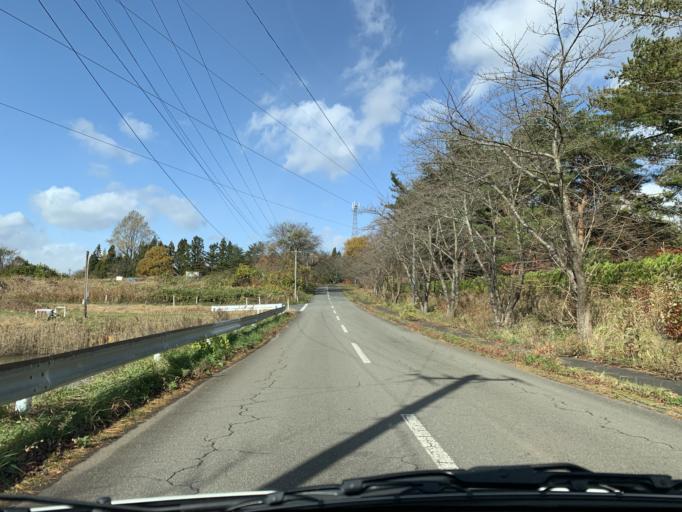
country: JP
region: Iwate
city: Mizusawa
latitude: 39.0366
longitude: 141.0840
